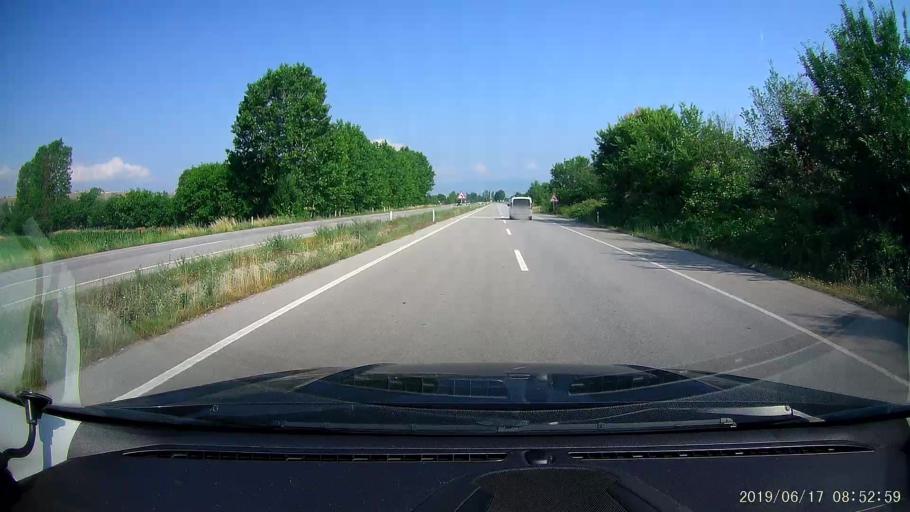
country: TR
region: Tokat
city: Erbaa
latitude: 40.7048
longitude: 36.4883
